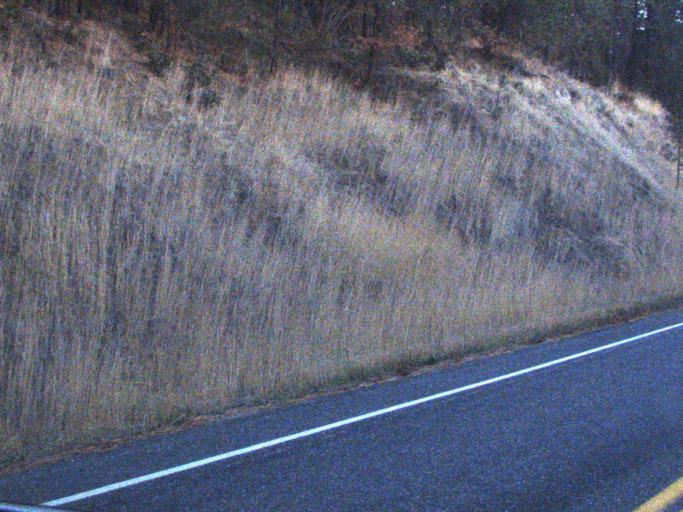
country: US
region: Washington
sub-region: Stevens County
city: Kettle Falls
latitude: 48.6237
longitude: -118.0726
